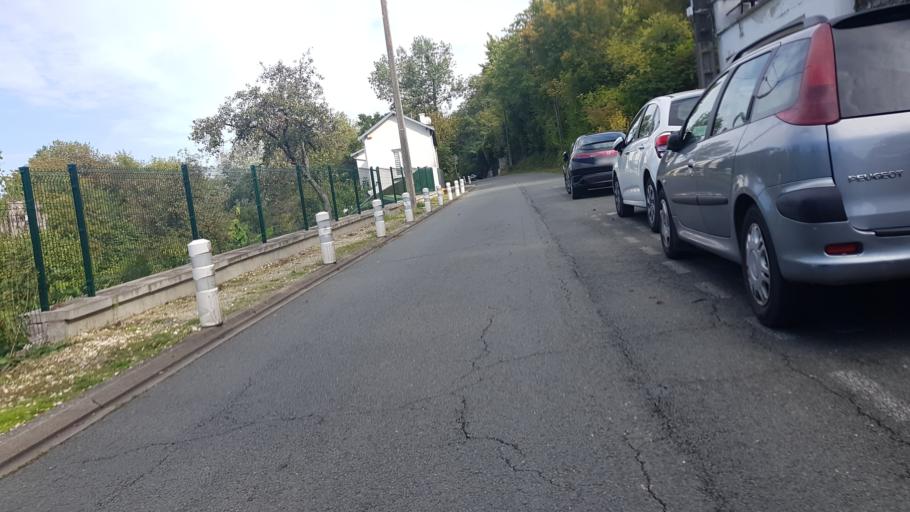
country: FR
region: Poitou-Charentes
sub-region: Departement de la Vienne
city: Chasseneuil-du-Poitou
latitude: 46.6145
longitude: 0.3580
